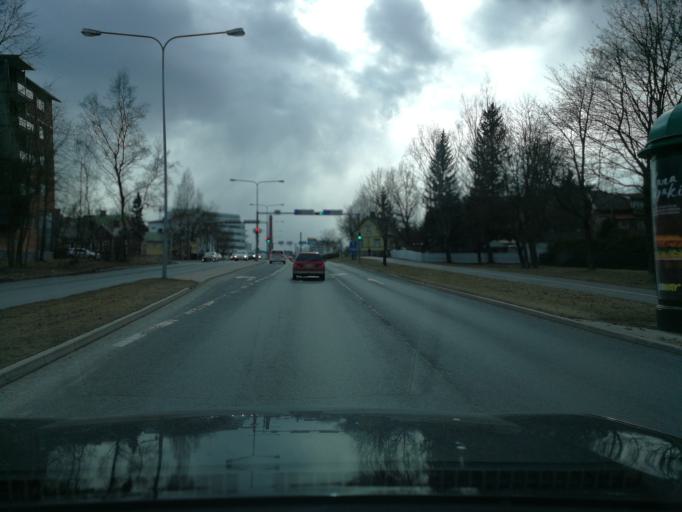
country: FI
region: Varsinais-Suomi
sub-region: Turku
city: Turku
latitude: 60.4566
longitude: 22.3017
